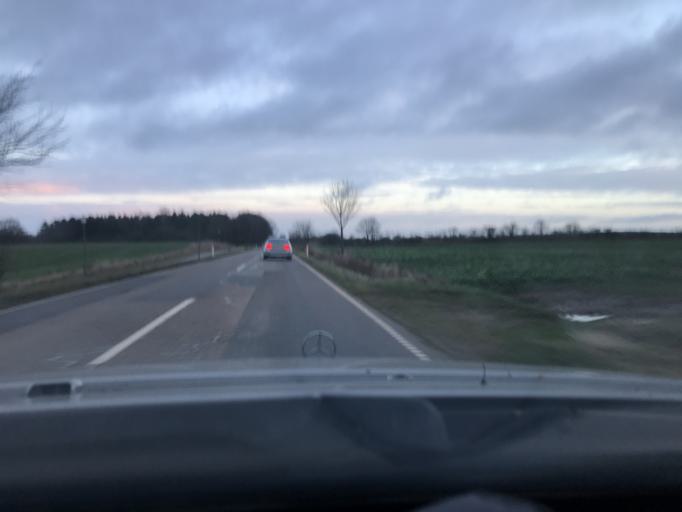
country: DK
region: South Denmark
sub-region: Sonderborg Kommune
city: Nordborg
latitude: 55.0565
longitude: 9.7251
